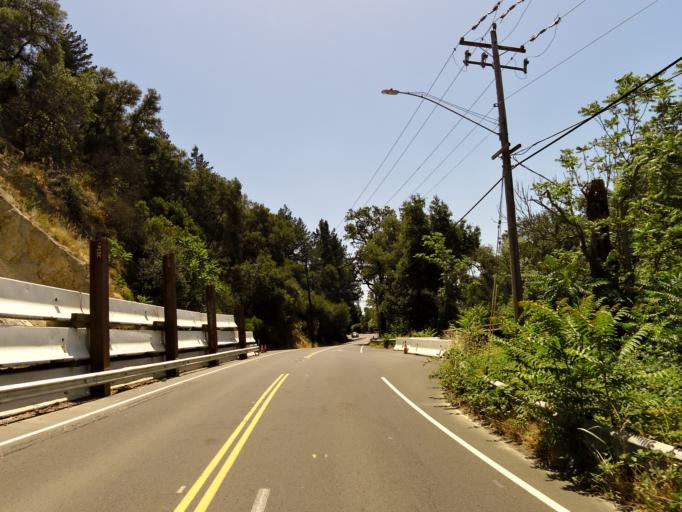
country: US
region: California
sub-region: Napa County
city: Deer Park
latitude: 38.5211
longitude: -122.4728
